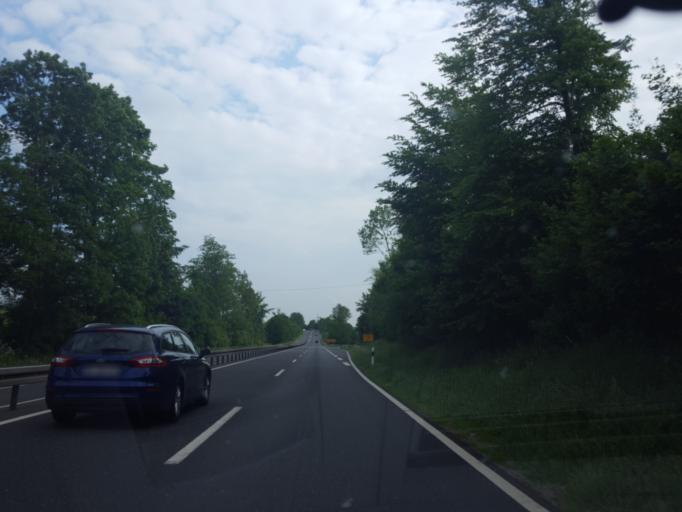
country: DE
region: Lower Saxony
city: Gittelde
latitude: 51.8193
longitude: 10.1898
